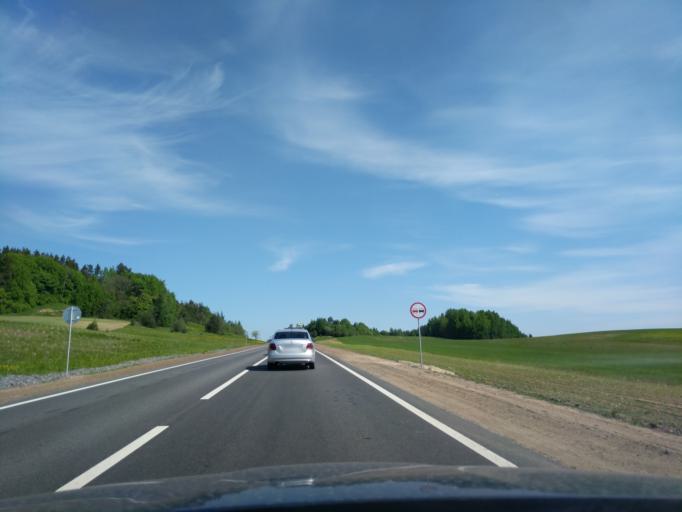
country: BY
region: Minsk
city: Bal'shavik
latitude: 54.0913
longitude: 27.5351
